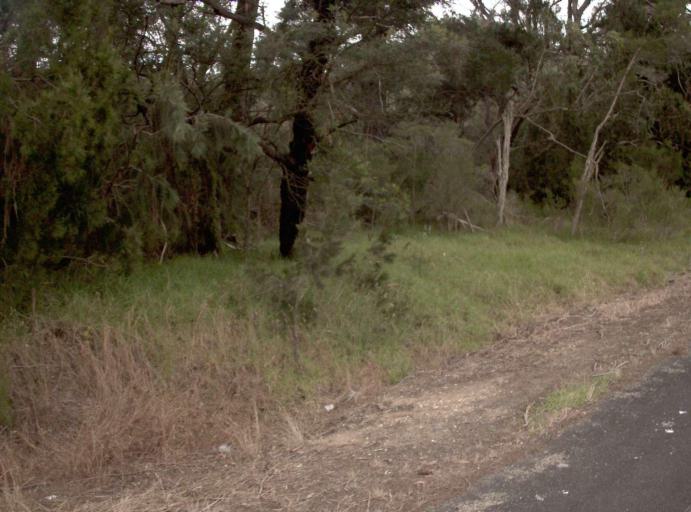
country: AU
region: Victoria
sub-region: Wellington
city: Sale
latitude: -38.1758
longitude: 147.0870
